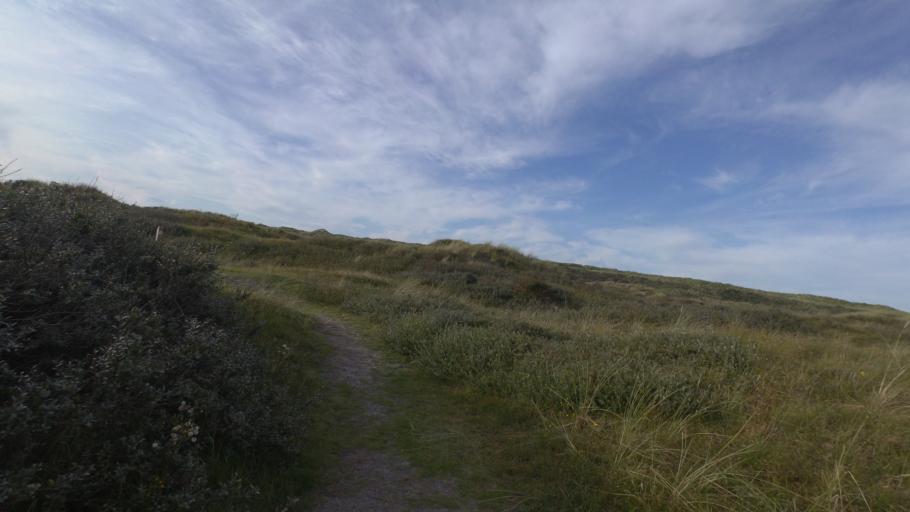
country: NL
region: Friesland
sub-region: Gemeente Ameland
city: Nes
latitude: 53.4600
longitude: 5.8154
